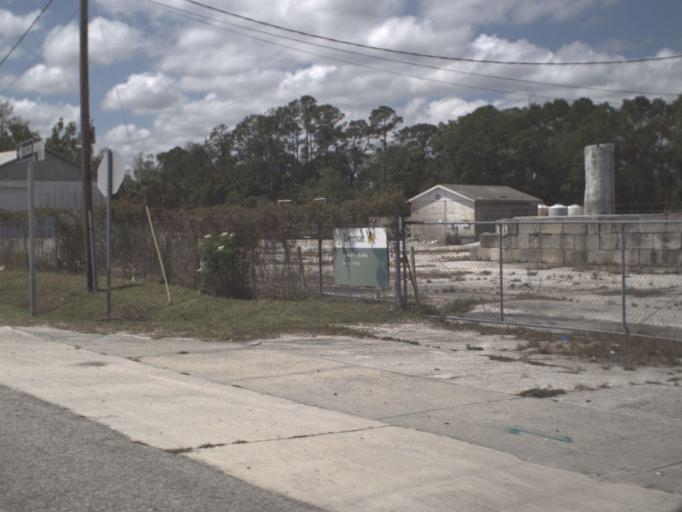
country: US
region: Florida
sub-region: Flagler County
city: Bunnell
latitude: 29.4779
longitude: -81.2674
